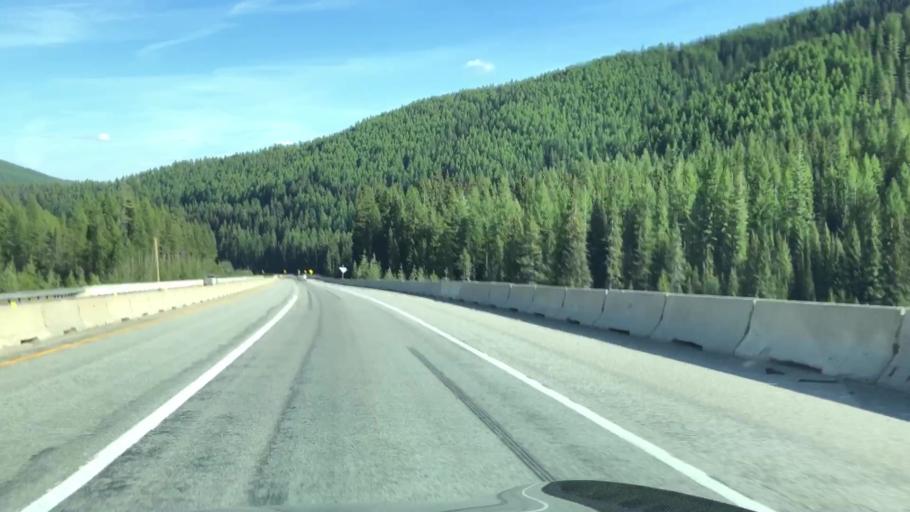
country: US
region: Idaho
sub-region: Shoshone County
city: Wallace
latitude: 47.4362
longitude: -115.6788
